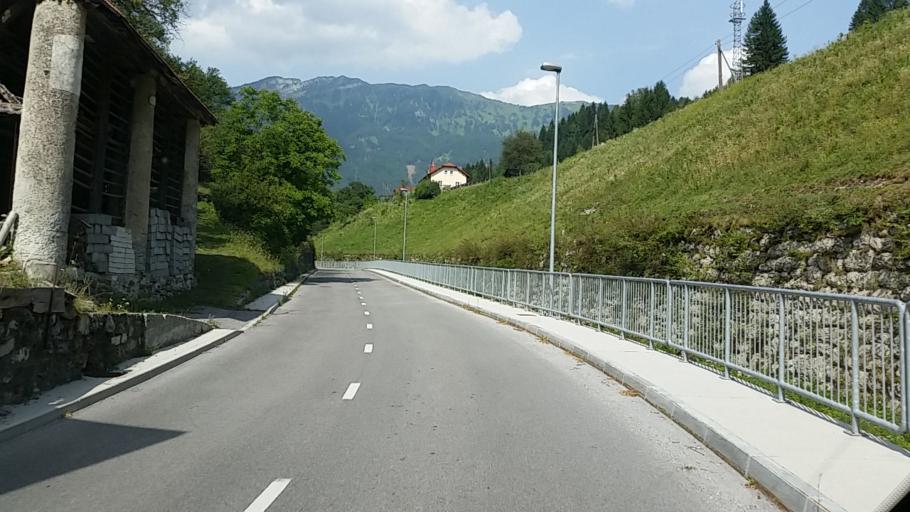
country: SI
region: Bohinj
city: Bohinjska Bistrica
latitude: 46.2073
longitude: 13.9645
